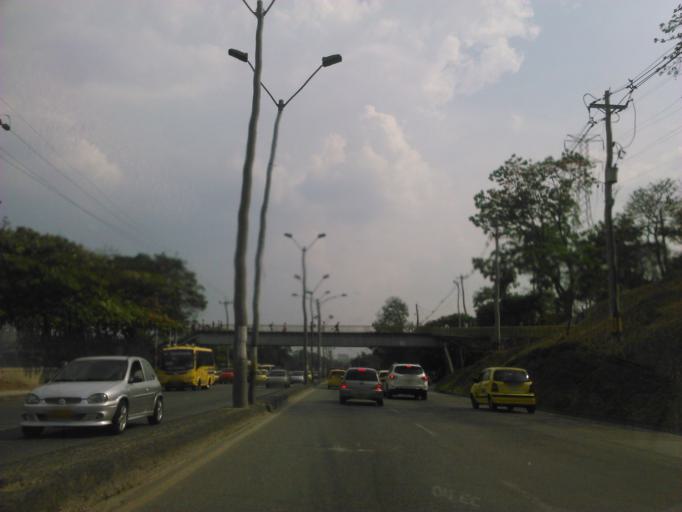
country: CO
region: Antioquia
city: Medellin
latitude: 6.2804
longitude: -75.5719
